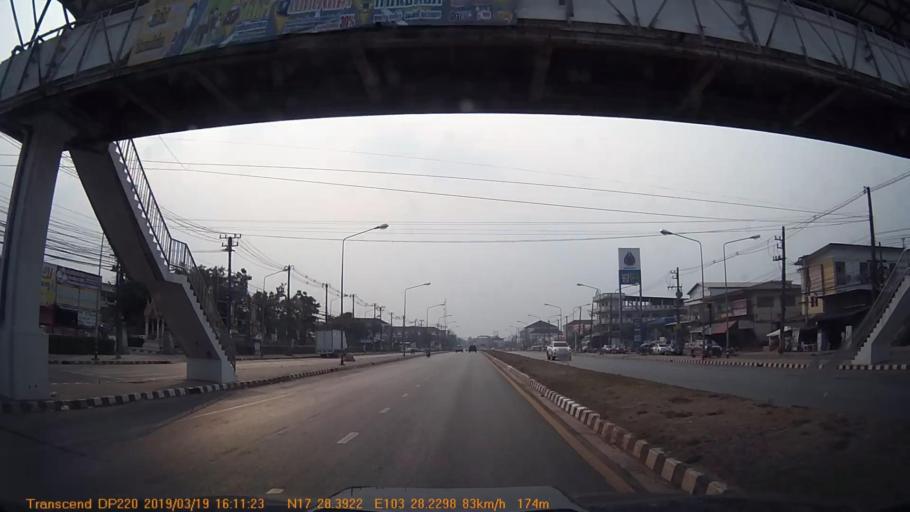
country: TH
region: Sakon Nakhon
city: Sawang Daen Din
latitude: 17.4734
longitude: 103.4698
